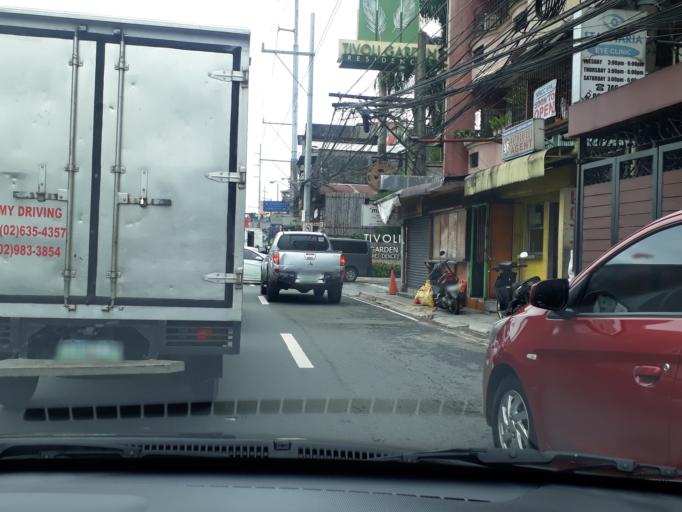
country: PH
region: Metro Manila
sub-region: Mandaluyong
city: Mandaluyong City
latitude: 14.5719
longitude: 121.0298
